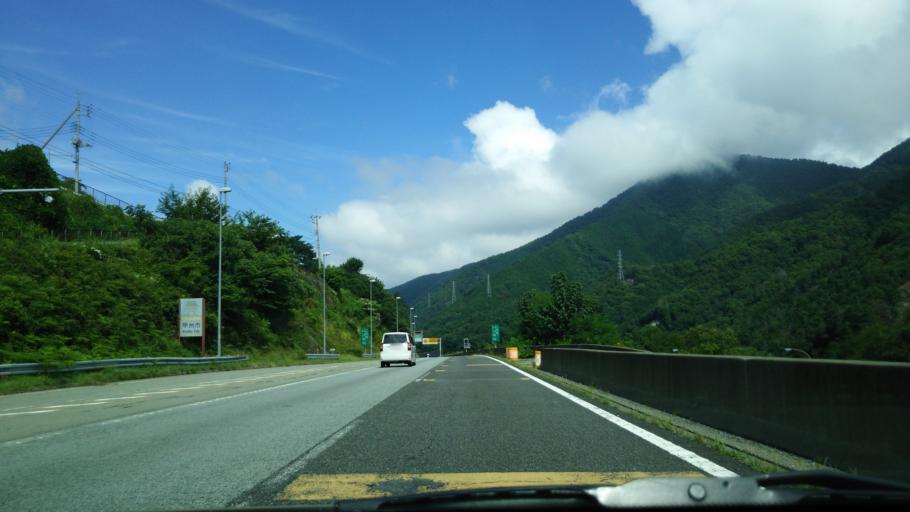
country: JP
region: Yamanashi
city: Enzan
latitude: 35.6371
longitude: 138.7764
